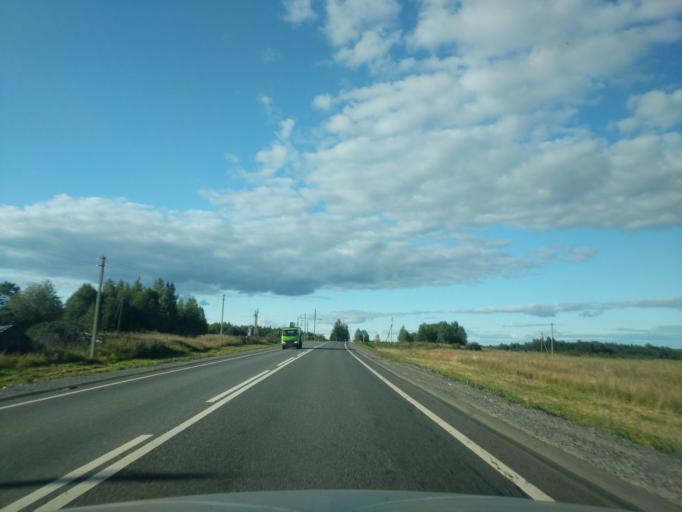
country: RU
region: Kostroma
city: Manturovo
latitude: 58.3348
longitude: 44.7159
